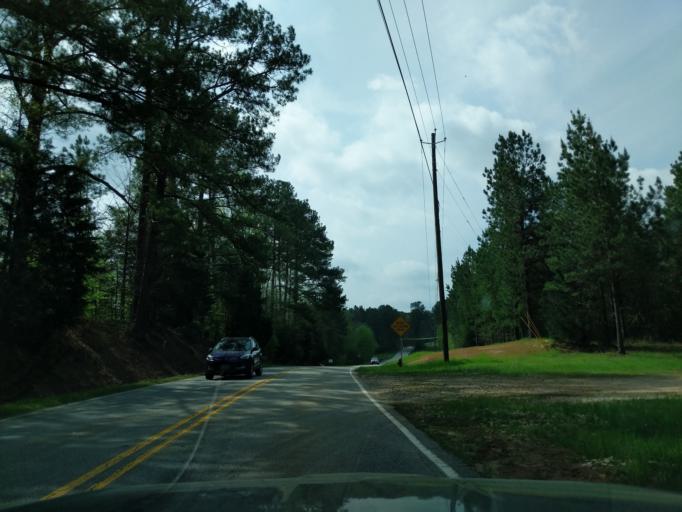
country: US
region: Georgia
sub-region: Columbia County
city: Appling
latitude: 33.5774
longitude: -82.3180
